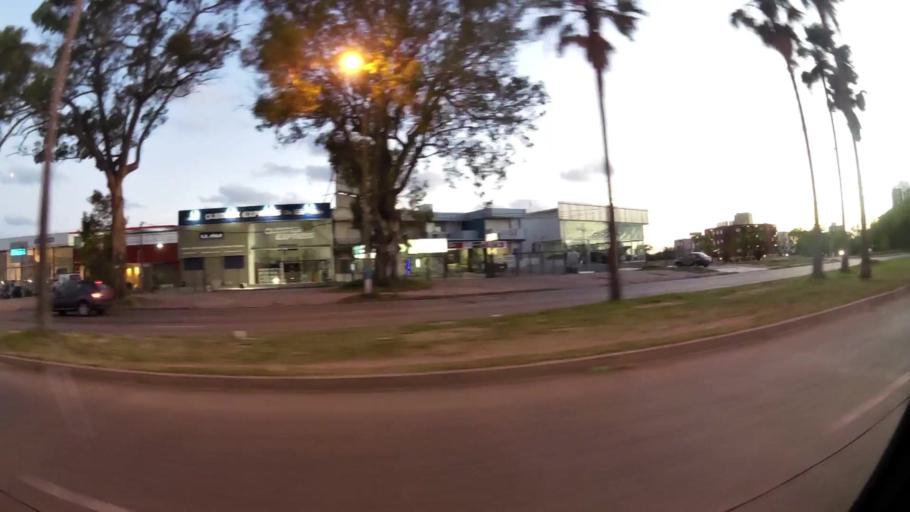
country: UY
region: Canelones
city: Paso de Carrasco
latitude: -34.8858
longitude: -56.0995
